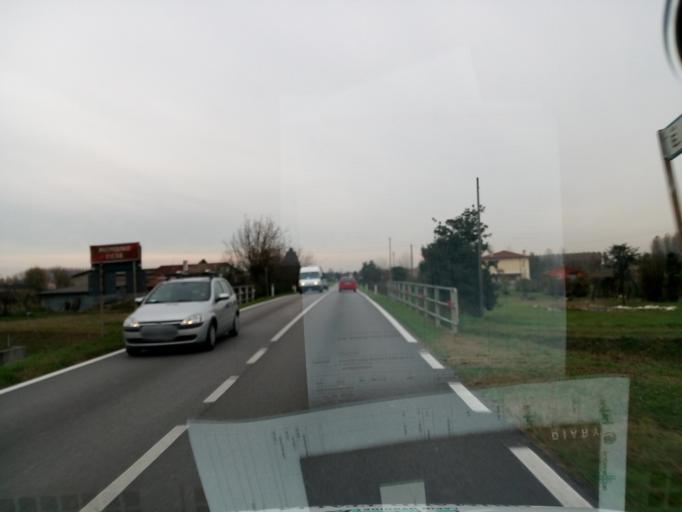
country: IT
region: Veneto
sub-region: Provincia di Padova
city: Piombino Dese
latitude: 45.5909
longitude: 12.0010
